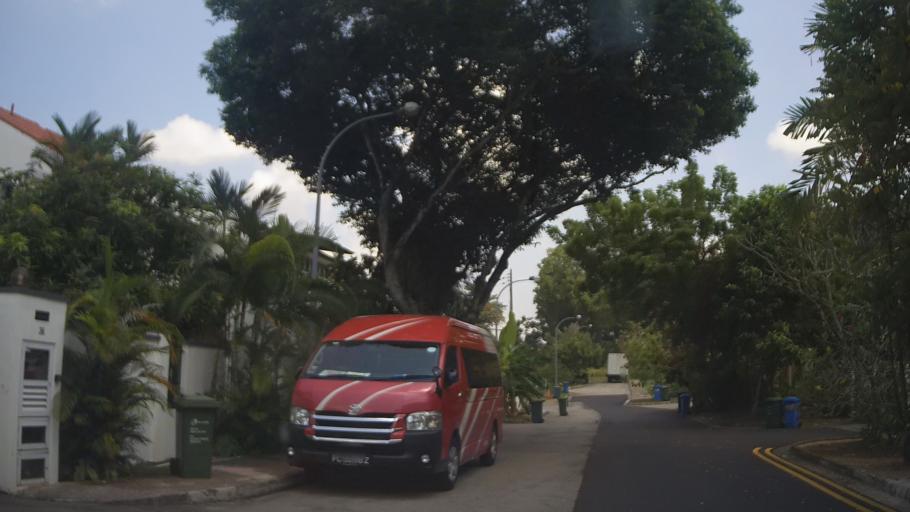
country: MY
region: Johor
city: Kampung Pasir Gudang Baru
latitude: 1.3982
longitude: 103.8738
